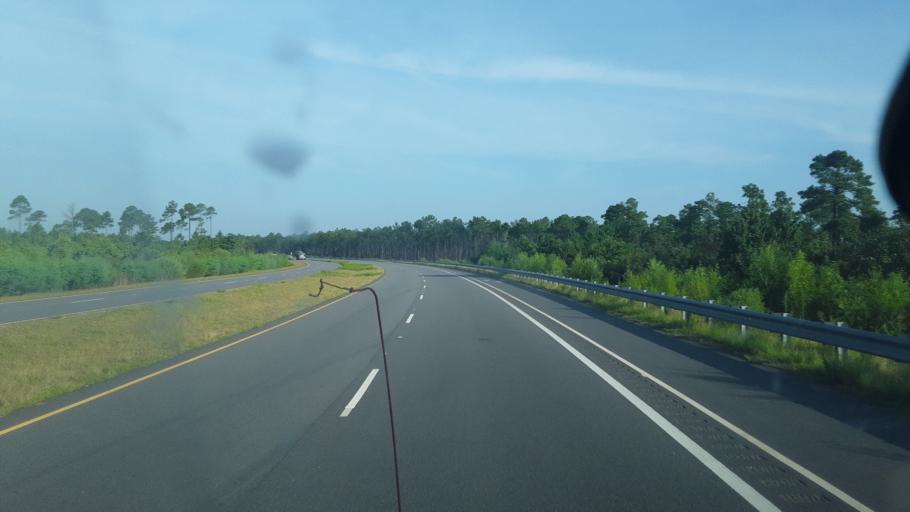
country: US
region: South Carolina
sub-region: Horry County
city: Forestbrook
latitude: 33.8010
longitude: -78.8841
